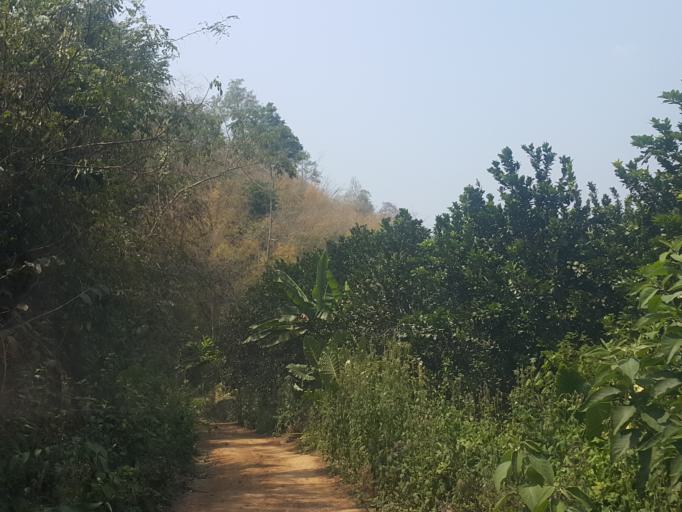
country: TH
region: Chiang Mai
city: Hang Dong
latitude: 18.7568
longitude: 98.8243
